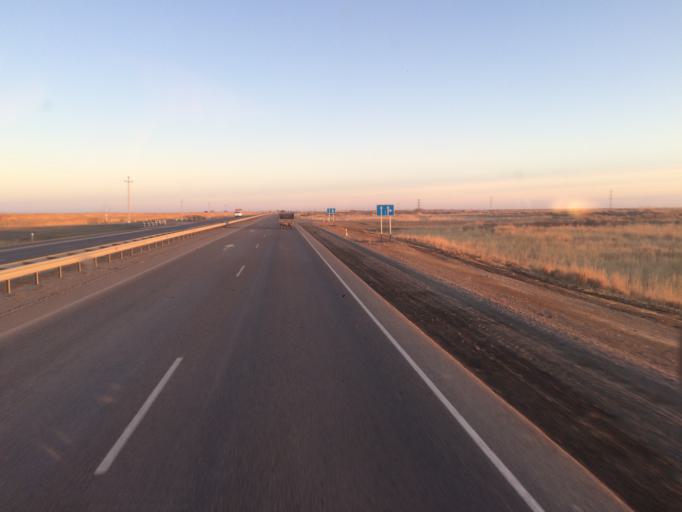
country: KZ
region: Qyzylorda
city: Shieli
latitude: 44.1703
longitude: 66.9076
